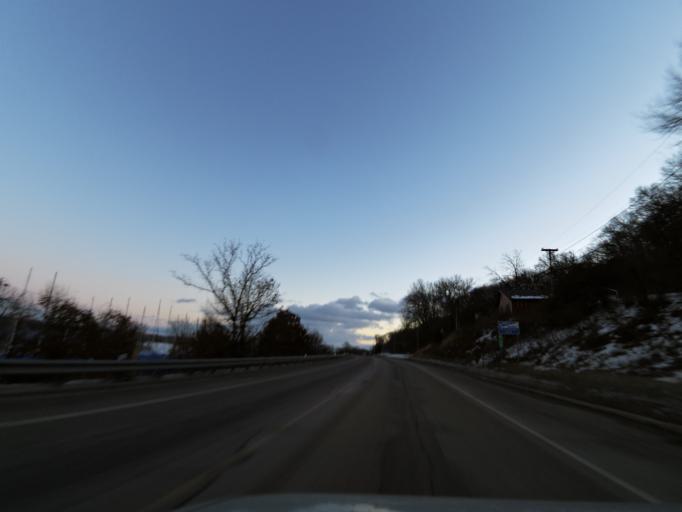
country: US
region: Minnesota
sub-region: Washington County
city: Bayport
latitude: 45.0055
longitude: -92.7796
